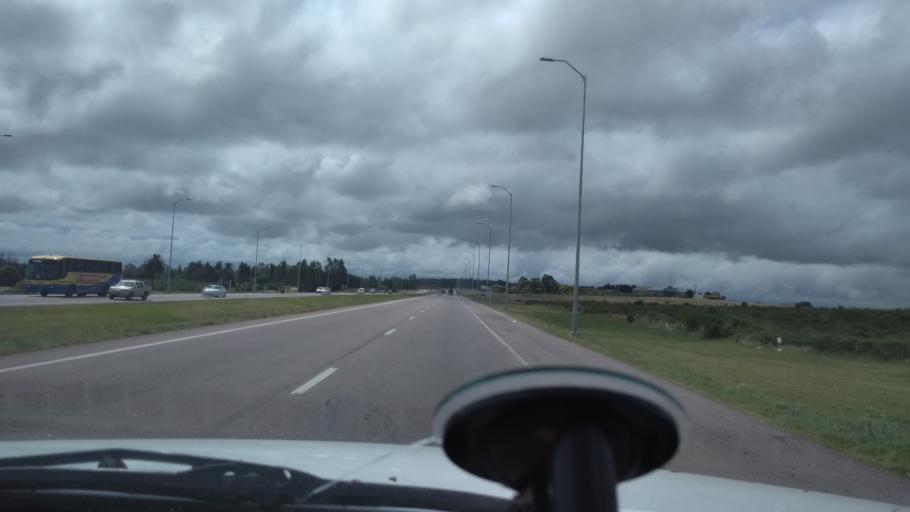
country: UY
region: Canelones
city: La Paz
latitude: -34.7943
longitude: -56.2683
